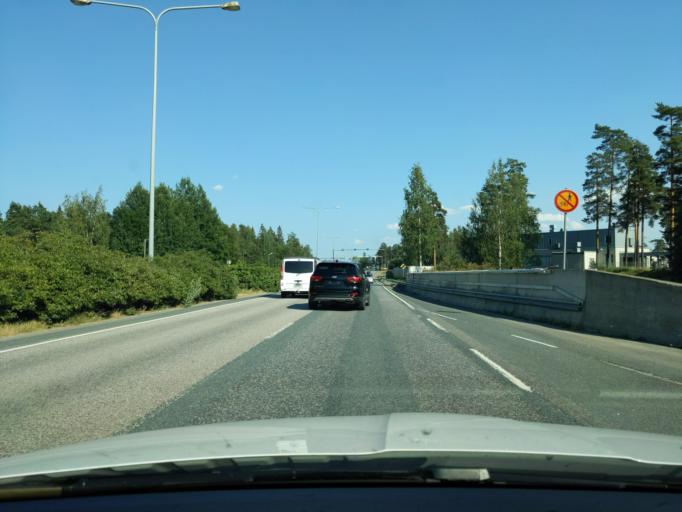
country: FI
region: Paijanne Tavastia
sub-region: Lahti
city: Lahti
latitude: 60.9798
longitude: 25.6041
